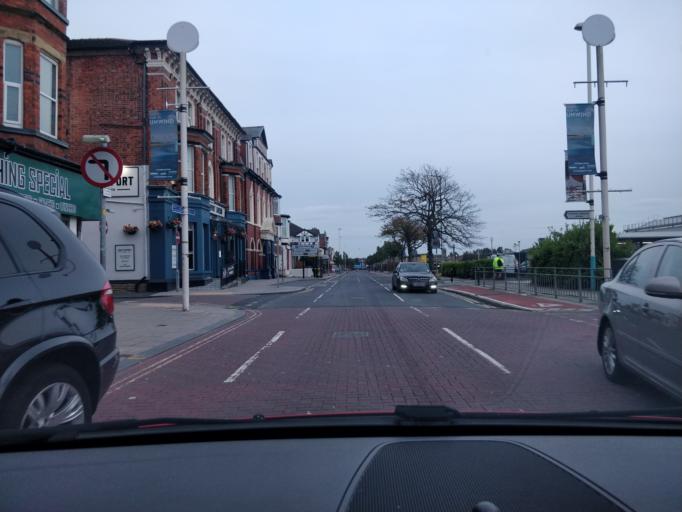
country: GB
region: England
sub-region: Sefton
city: Southport
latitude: 53.6473
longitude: -3.0021
